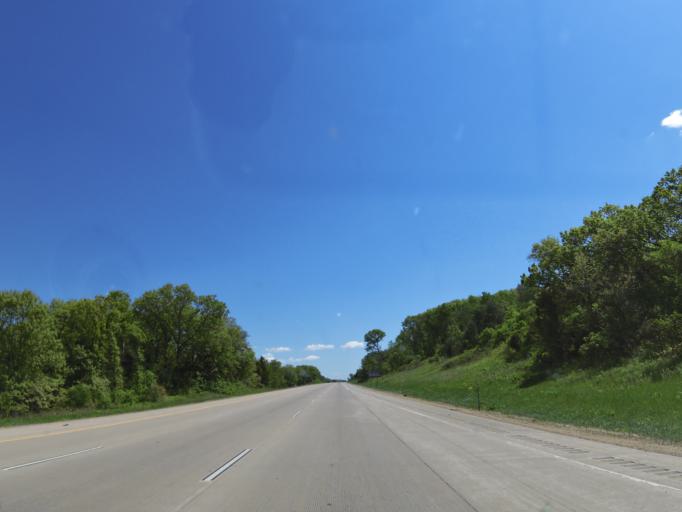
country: US
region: Wisconsin
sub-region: Columbia County
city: Poynette
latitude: 43.3857
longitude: -89.4658
